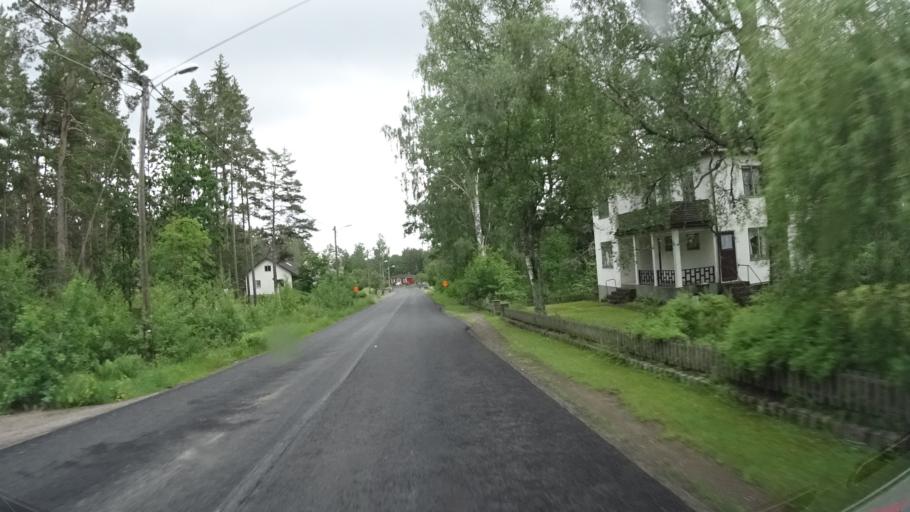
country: SE
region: Kalmar
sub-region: Hogsby Kommun
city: Hoegsby
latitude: 57.4041
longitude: 16.1837
